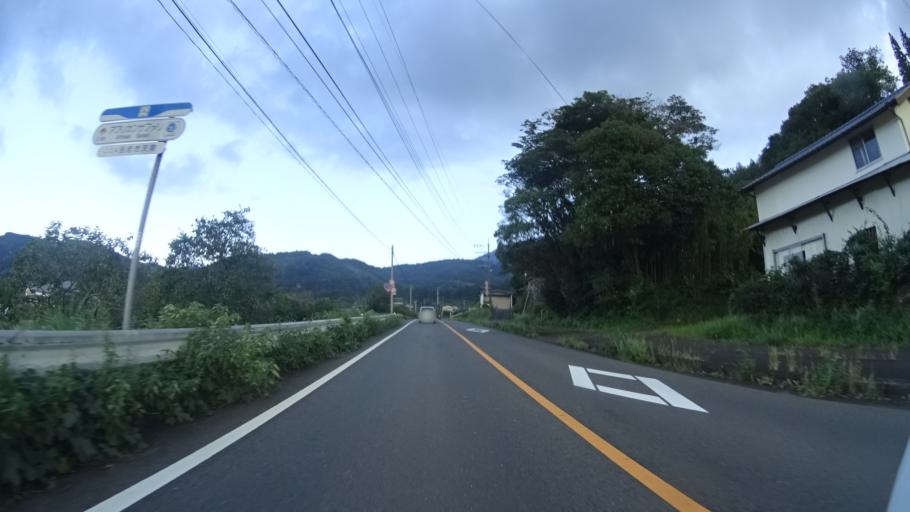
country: JP
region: Oita
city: Beppu
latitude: 33.3367
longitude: 131.4046
